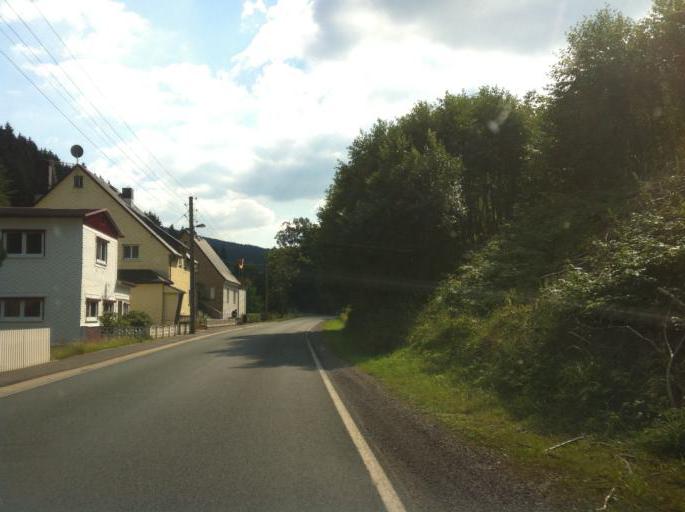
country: DE
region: Thuringia
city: Goldisthal
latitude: 50.5340
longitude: 11.0155
